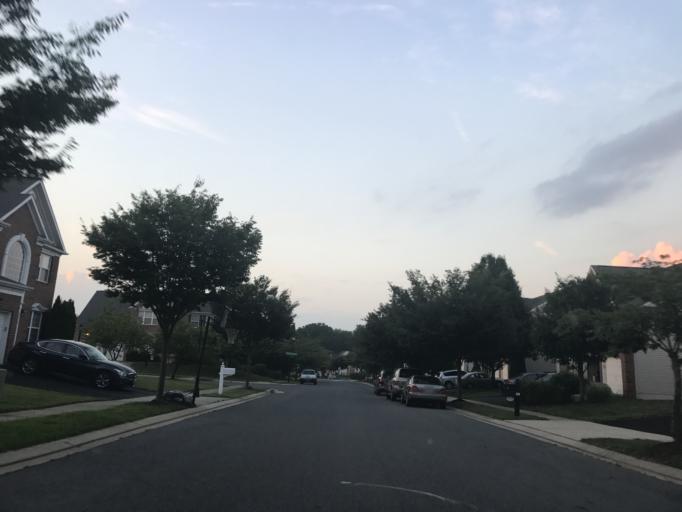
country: US
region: Maryland
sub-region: Baltimore County
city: White Marsh
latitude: 39.4055
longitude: -76.4293
